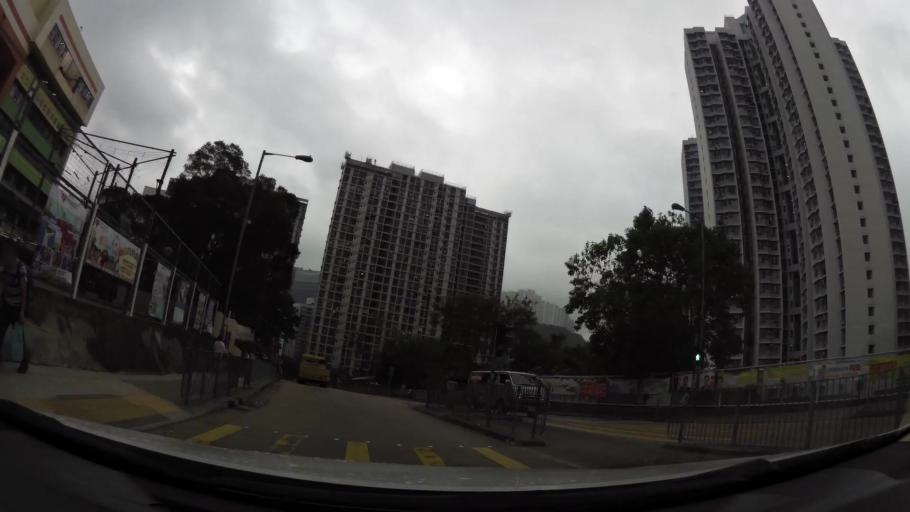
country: HK
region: Tsuen Wan
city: Tsuen Wan
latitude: 22.3643
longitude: 114.1282
